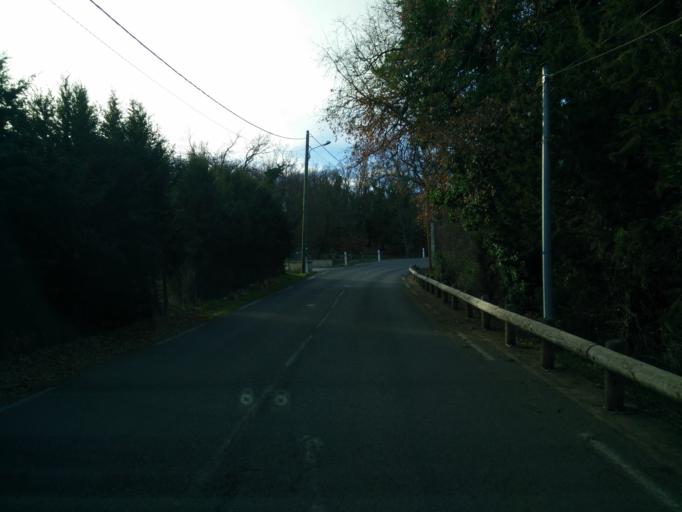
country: FR
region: Provence-Alpes-Cote d'Azur
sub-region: Departement des Alpes-Maritimes
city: Saint-Cezaire-sur-Siagne
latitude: 43.6473
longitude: 6.8026
